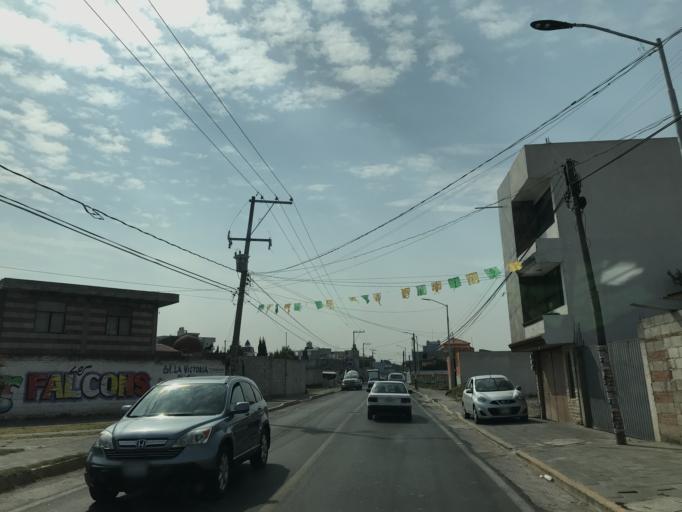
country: MX
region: Tlaxcala
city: Tenancingo
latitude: 19.1439
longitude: -98.1944
